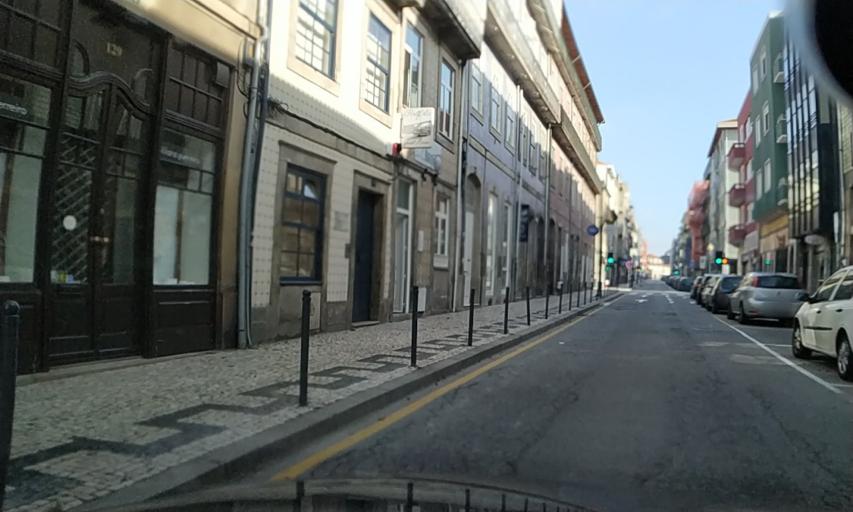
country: PT
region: Porto
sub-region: Porto
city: Porto
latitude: 41.1490
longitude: -8.6207
